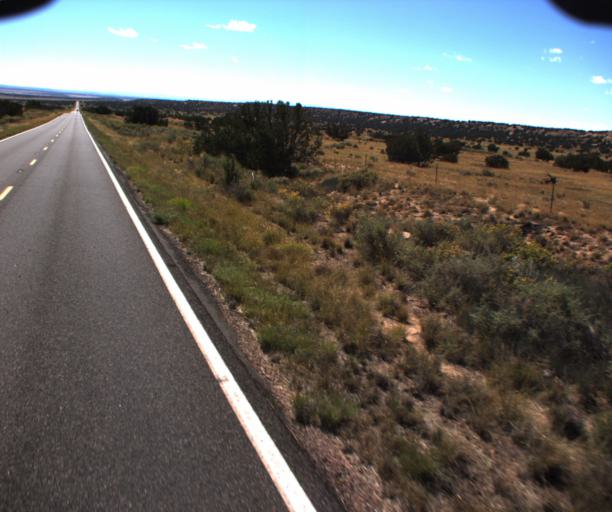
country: US
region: Arizona
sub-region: Apache County
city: Saint Johns
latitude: 34.8131
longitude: -109.2377
